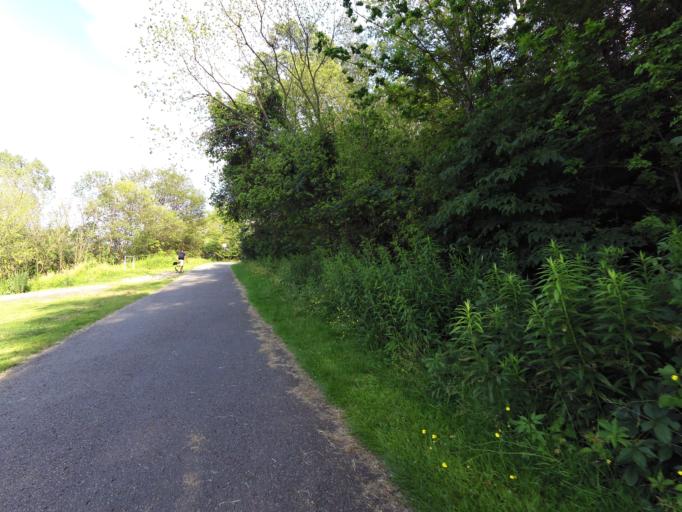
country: CA
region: Ontario
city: Etobicoke
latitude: 43.6461
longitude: -79.4948
